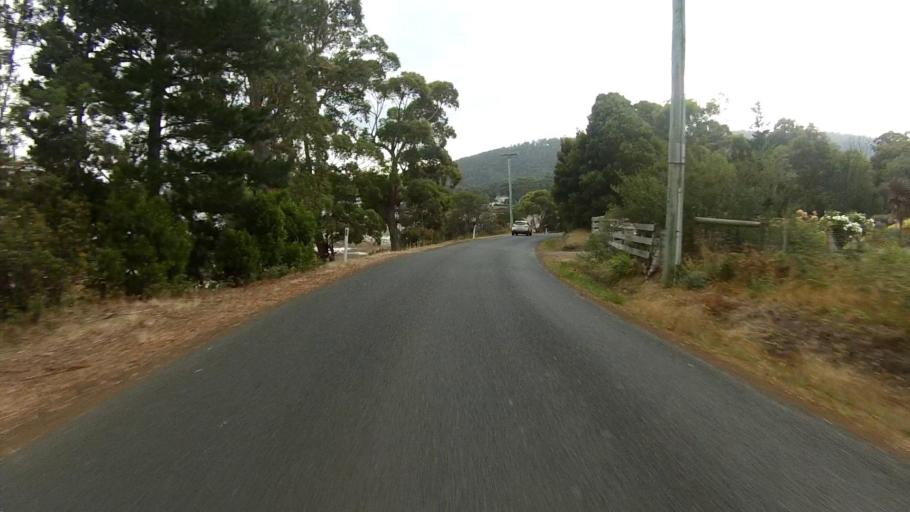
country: AU
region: Tasmania
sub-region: Huon Valley
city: Cygnet
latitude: -43.2122
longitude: 147.1138
